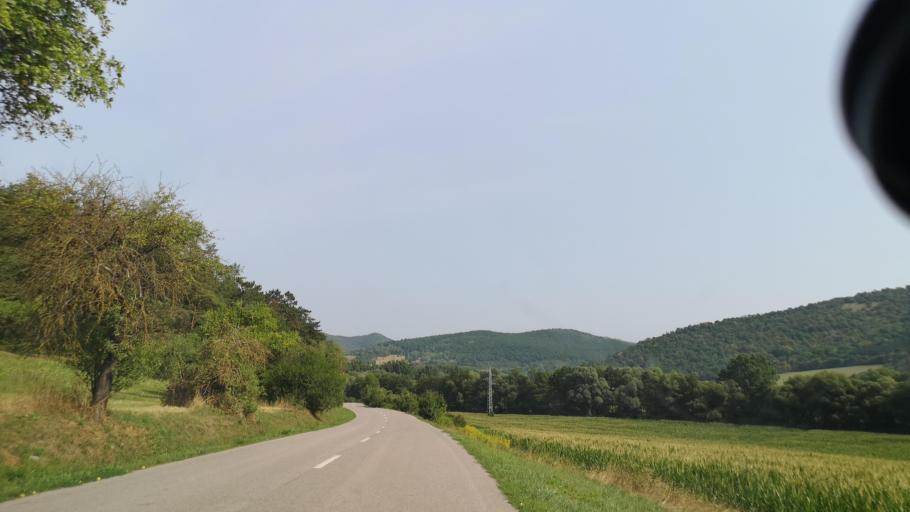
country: SK
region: Banskobystricky
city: Revuca
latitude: 48.6141
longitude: 20.2409
